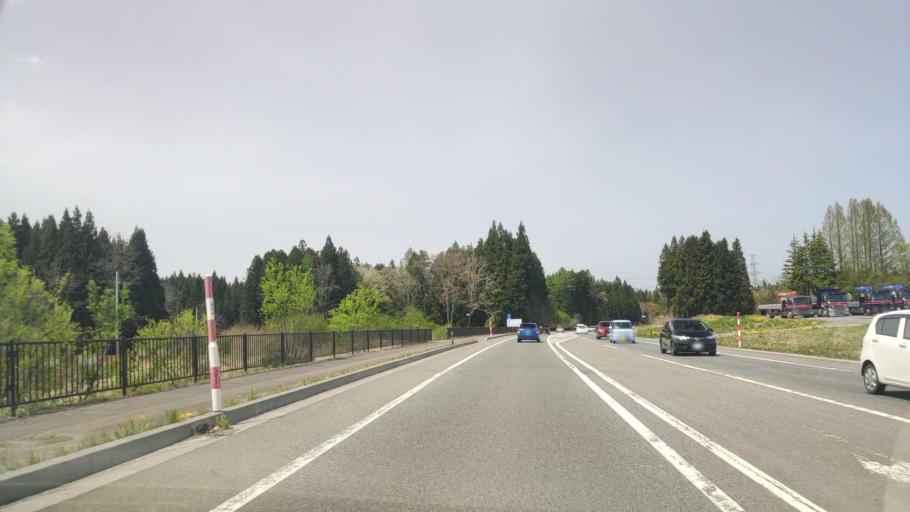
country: JP
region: Aomori
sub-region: Misawa Shi
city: Inuotose
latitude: 40.6778
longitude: 141.1731
